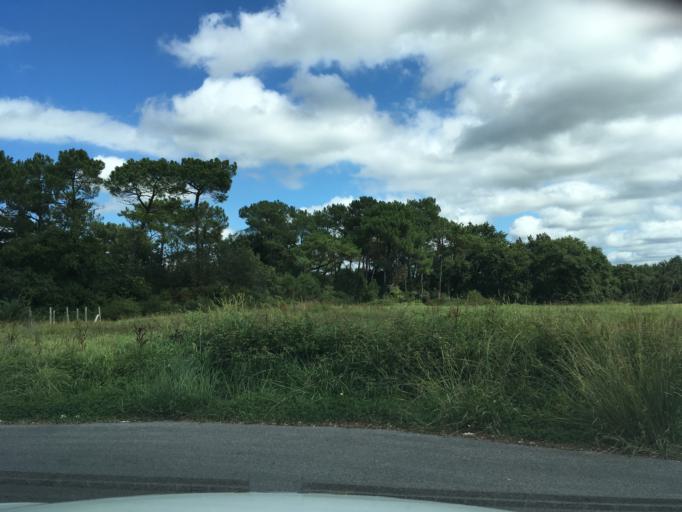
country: FR
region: Aquitaine
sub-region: Departement des Pyrenees-Atlantiques
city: Mouguerre
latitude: 43.5074
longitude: -1.4295
